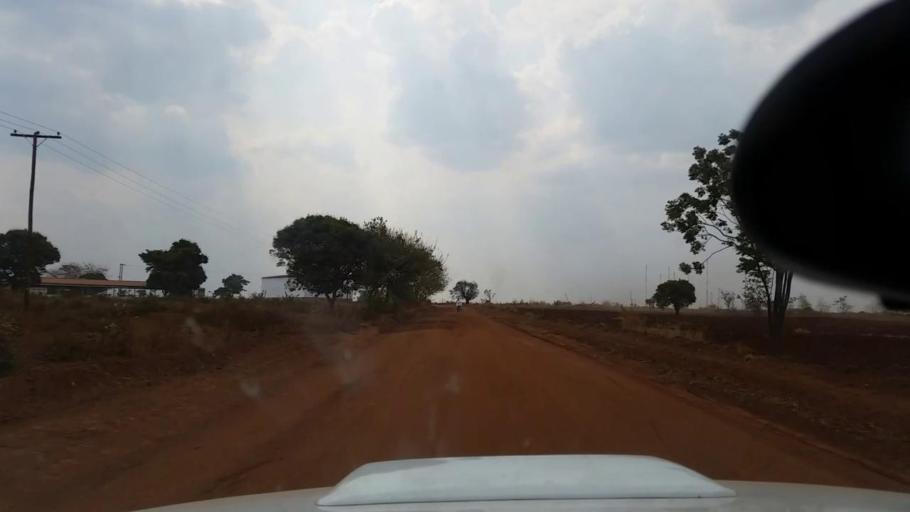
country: MW
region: Central Region
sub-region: Lilongwe District
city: Lilongwe
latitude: -13.7938
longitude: 33.7710
